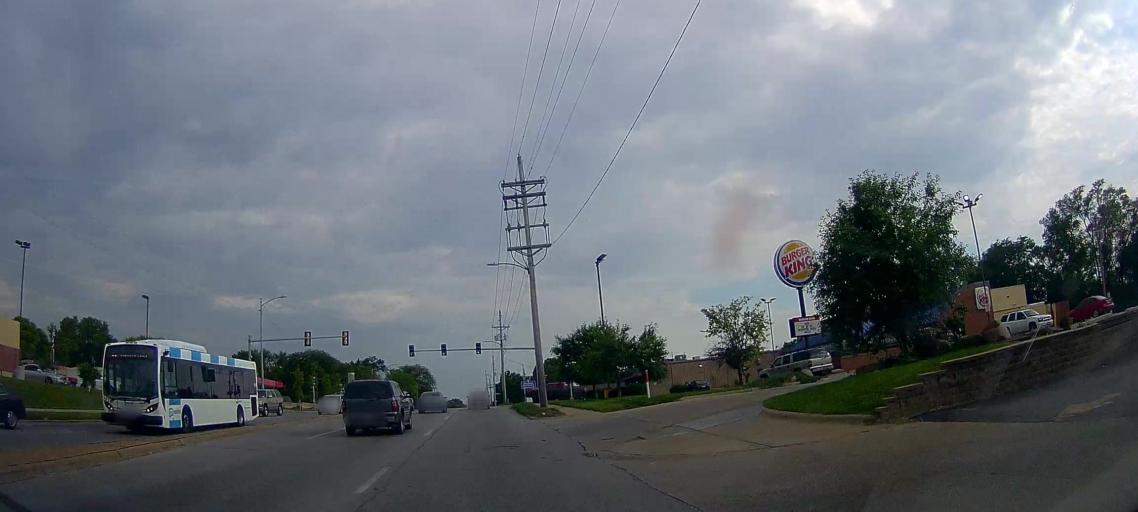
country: US
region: Nebraska
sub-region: Douglas County
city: Ralston
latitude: 41.2769
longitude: -96.0239
